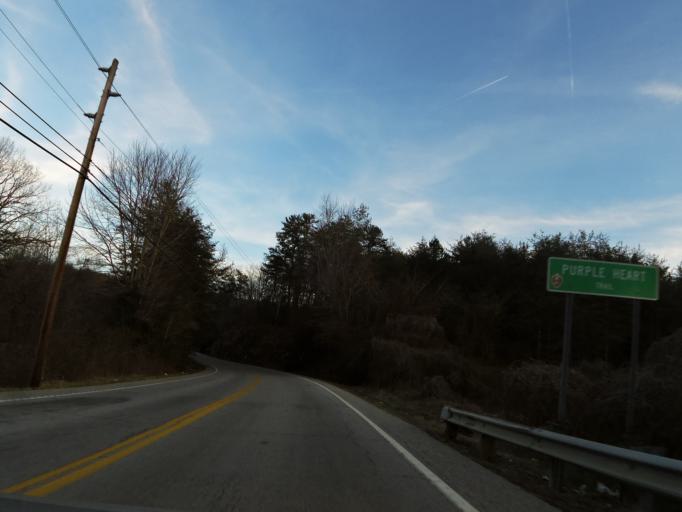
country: US
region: Tennessee
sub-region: Roane County
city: Rockwood
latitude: 35.8509
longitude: -84.7337
